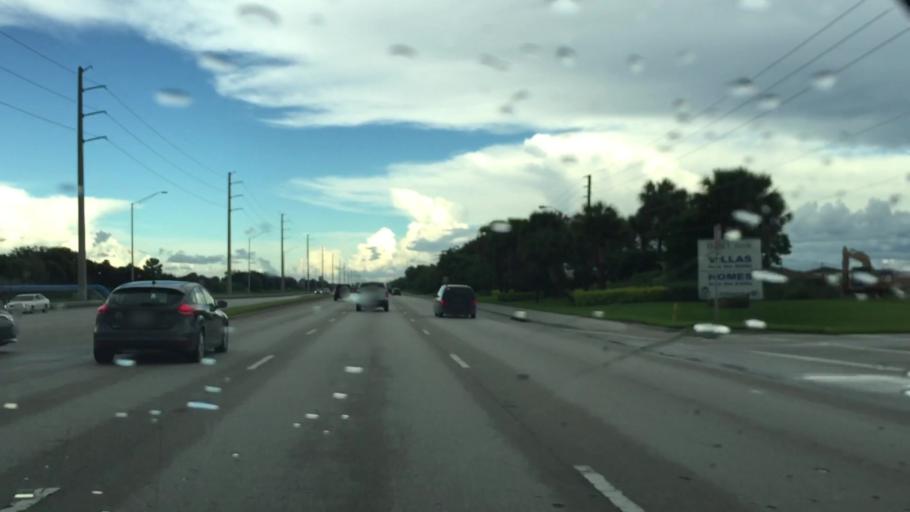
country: US
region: Florida
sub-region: Collier County
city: Vineyards
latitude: 26.2730
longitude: -81.6819
